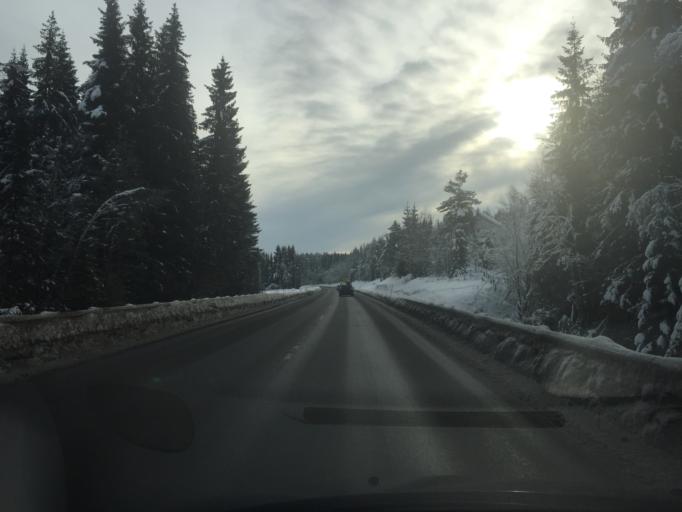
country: NO
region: Hedmark
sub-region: Trysil
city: Innbygda
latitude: 61.2756
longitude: 12.2896
